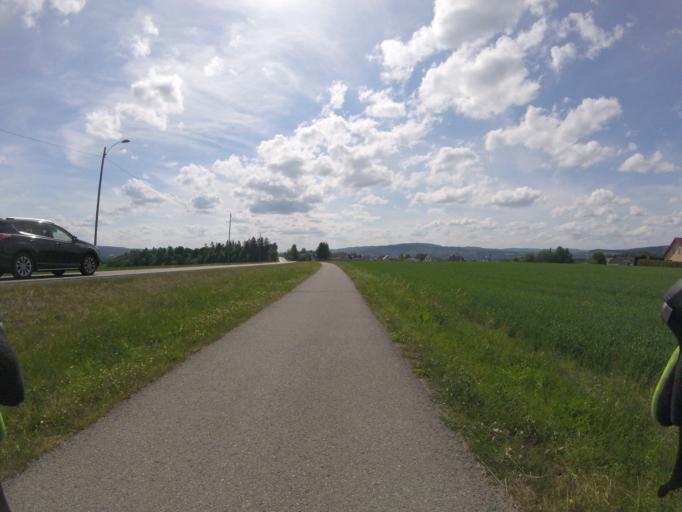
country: NO
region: Akershus
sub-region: Skedsmo
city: Lillestrom
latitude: 59.9866
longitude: 11.0480
